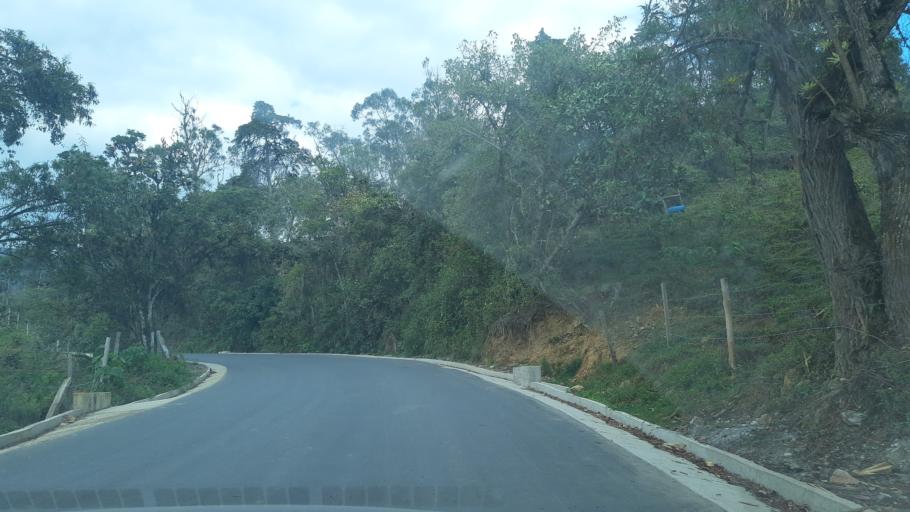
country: CO
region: Boyaca
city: Garagoa
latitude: 5.0880
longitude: -73.3478
